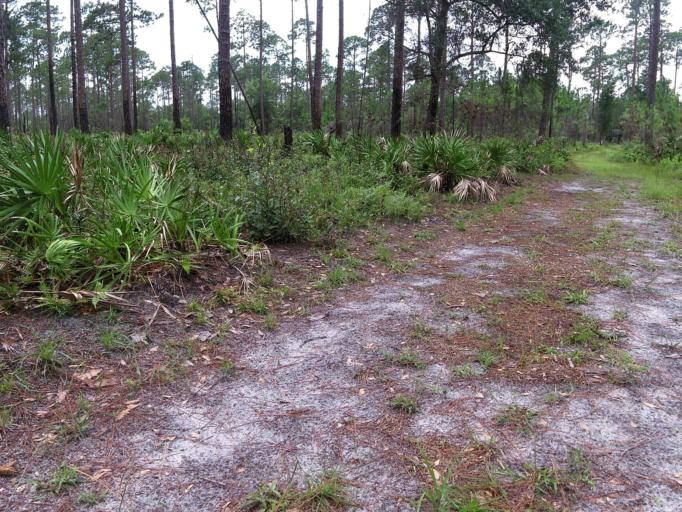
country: US
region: Florida
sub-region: Clay County
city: Green Cove Springs
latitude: 29.9717
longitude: -81.6365
